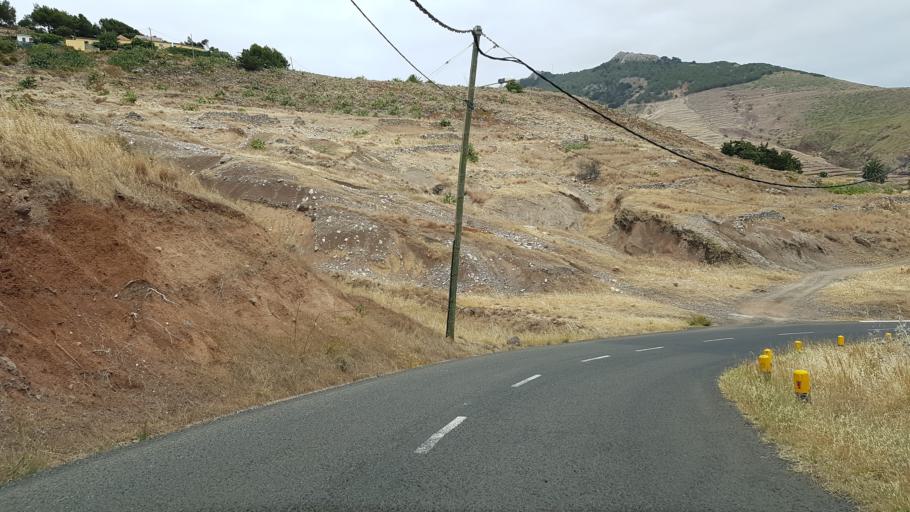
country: PT
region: Madeira
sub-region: Porto Santo
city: Vila de Porto Santo
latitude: 33.0704
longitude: -16.3147
